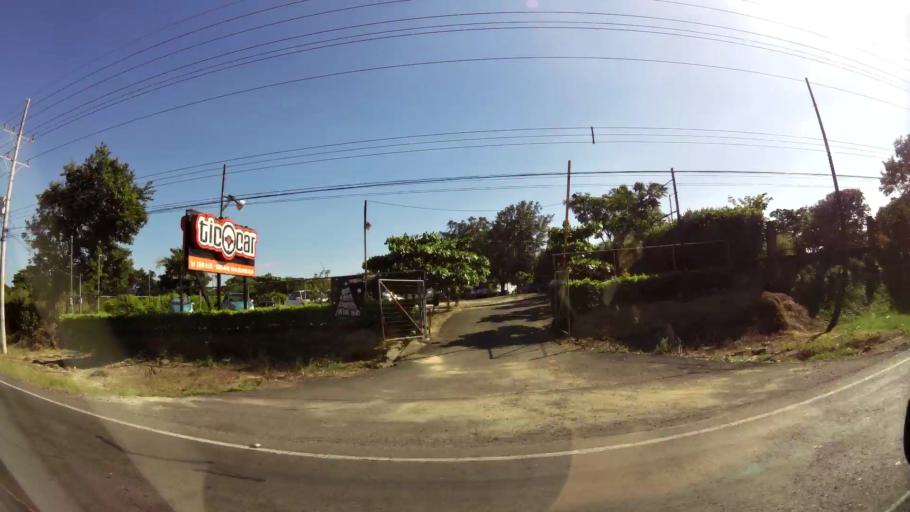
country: CR
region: Guanacaste
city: Liberia
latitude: 10.6128
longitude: -85.4920
